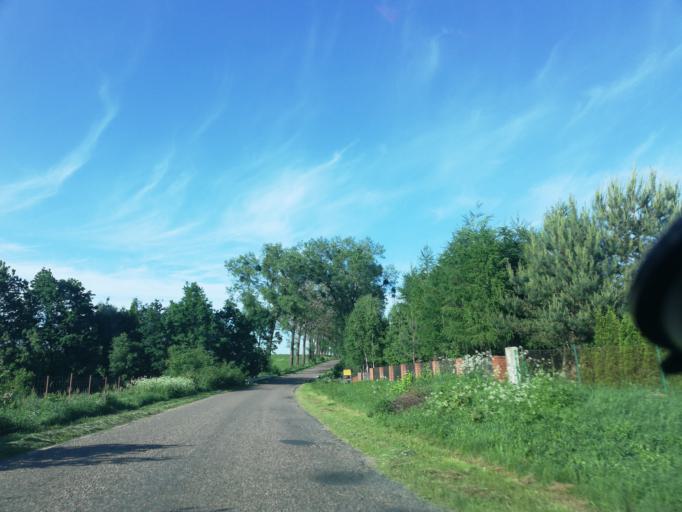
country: PL
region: Kujawsko-Pomorskie
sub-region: Powiat golubsko-dobrzynski
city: Golub-Dobrzyn
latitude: 53.0282
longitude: 19.0679
